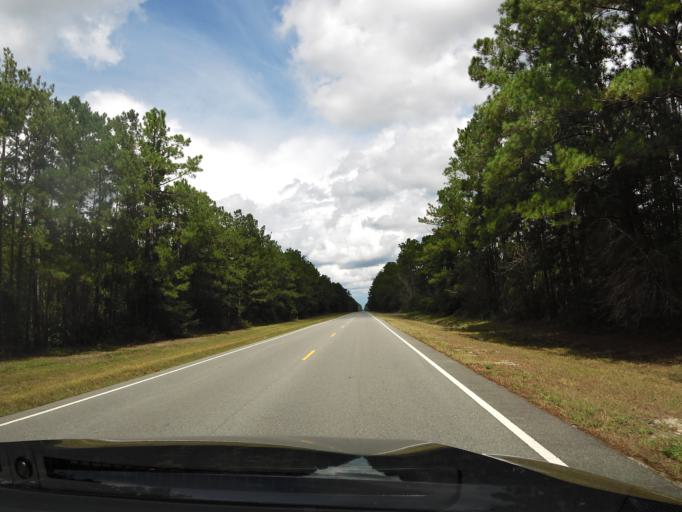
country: US
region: Georgia
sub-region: Brantley County
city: Nahunta
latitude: 31.0508
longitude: -82.0172
